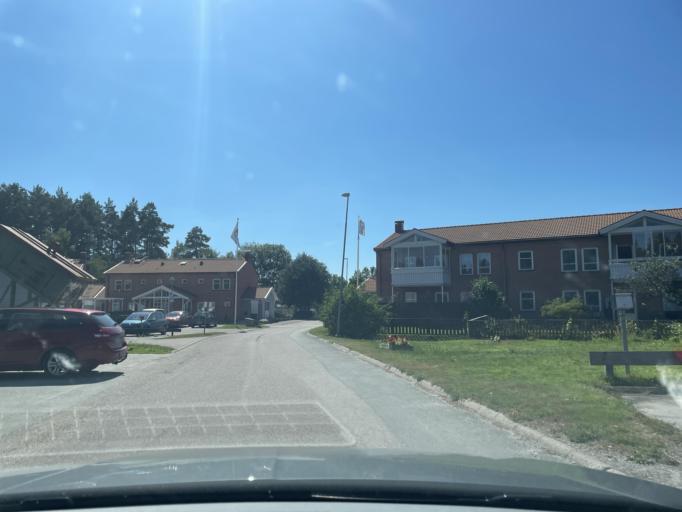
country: SE
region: Stockholm
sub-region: Sigtuna Kommun
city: Rosersberg
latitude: 59.5854
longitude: 17.8830
